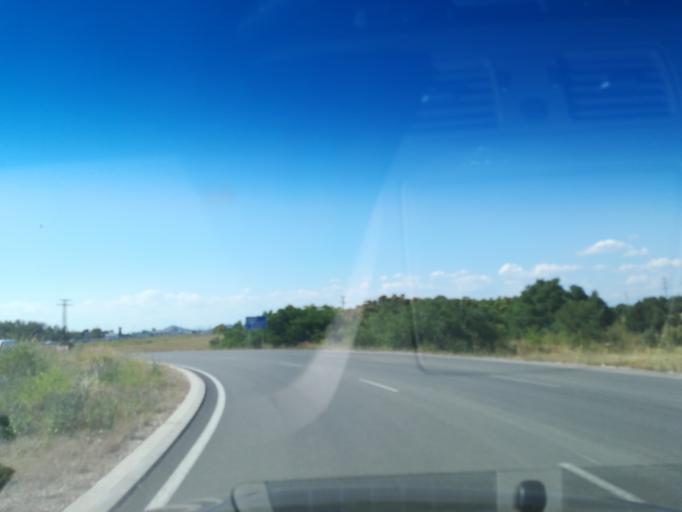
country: BG
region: Plovdiv
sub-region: Obshtina Plovdiv
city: Plovdiv
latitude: 42.0806
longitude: 24.8023
